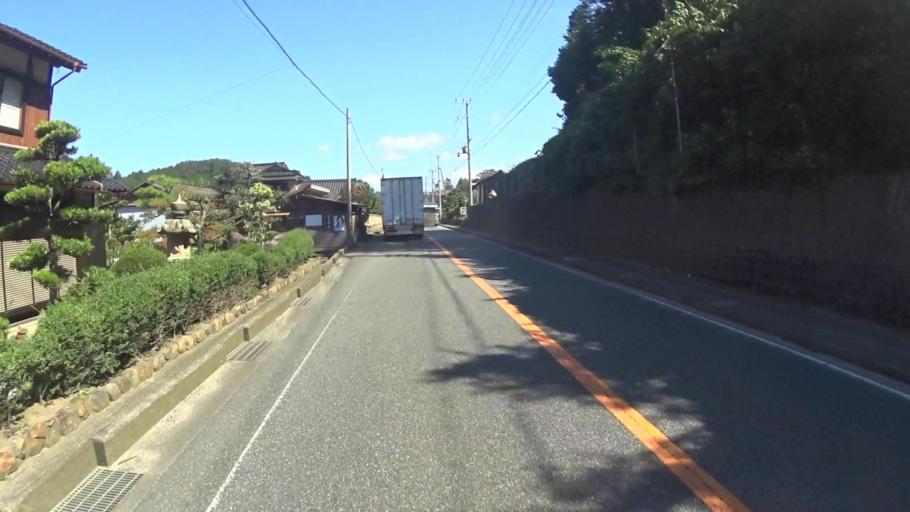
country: JP
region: Kyoto
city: Ayabe
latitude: 35.3536
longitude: 135.3115
